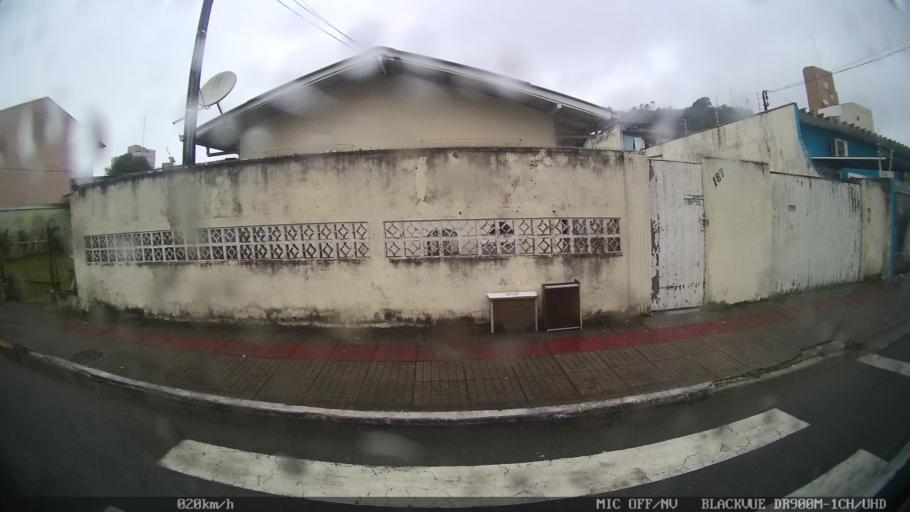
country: BR
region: Santa Catarina
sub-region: Itajai
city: Itajai
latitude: -26.9132
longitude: -48.6634
